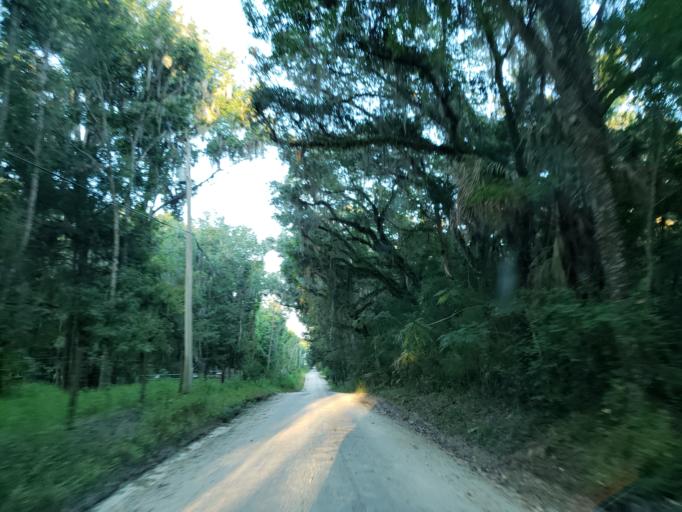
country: US
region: Florida
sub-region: Marion County
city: Citra
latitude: 29.4843
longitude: -82.2498
